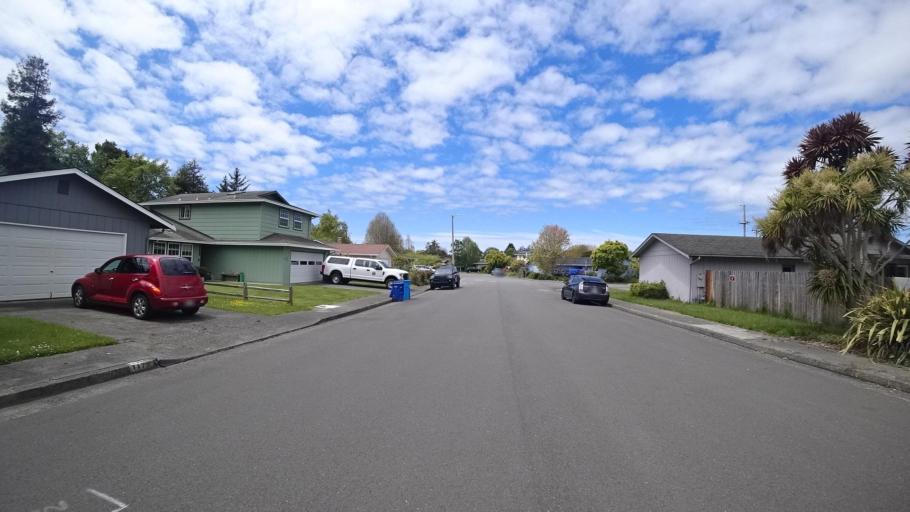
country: US
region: California
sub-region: Humboldt County
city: Arcata
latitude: 40.8839
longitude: -124.0841
